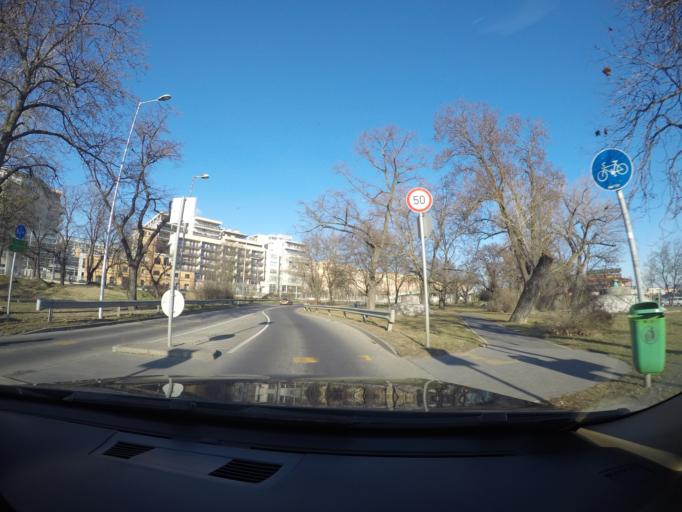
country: HU
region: Budapest
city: Budapest III. keruelet
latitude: 47.5317
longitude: 19.0437
